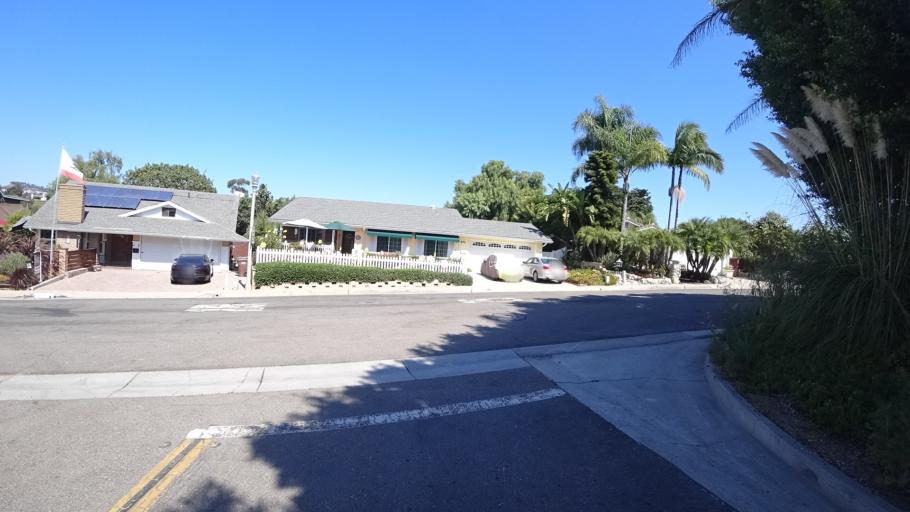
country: US
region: California
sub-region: Orange County
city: San Clemente
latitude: 33.4455
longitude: -117.6341
